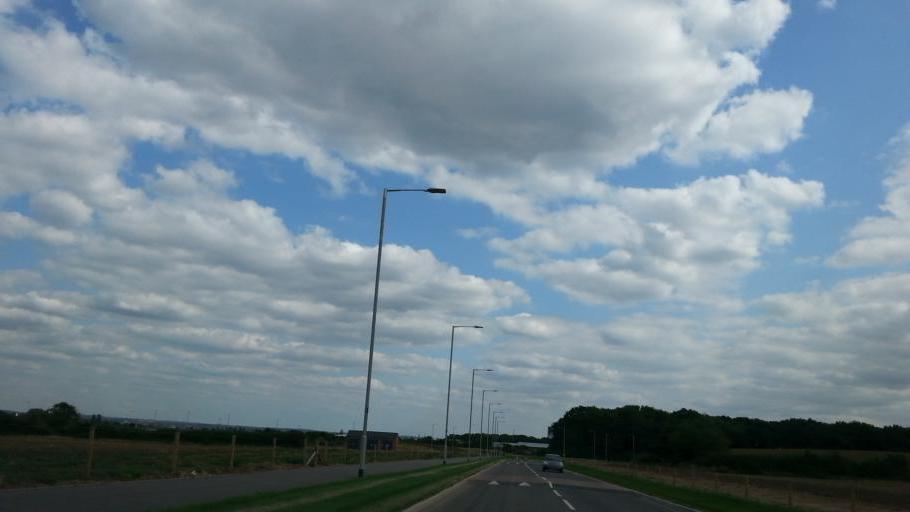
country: GB
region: England
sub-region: Leicestershire
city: Enderby
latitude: 52.6131
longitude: -1.2076
